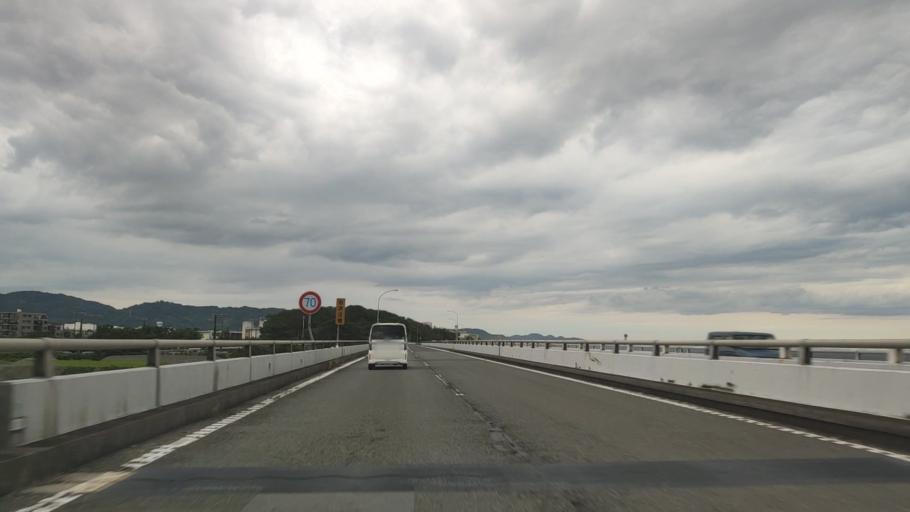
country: JP
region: Kanagawa
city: Odawara
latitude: 35.2611
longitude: 139.1833
